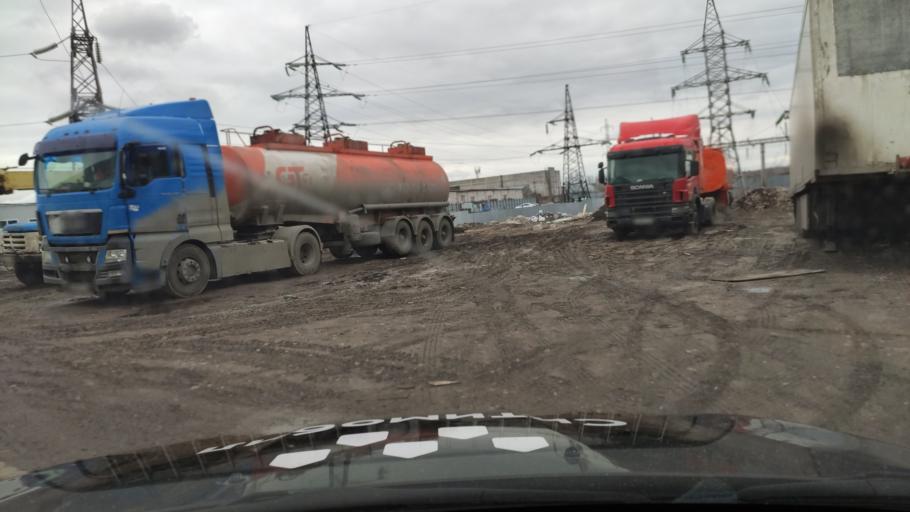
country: RU
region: Samara
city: Tol'yatti
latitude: 53.5266
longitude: 49.4686
